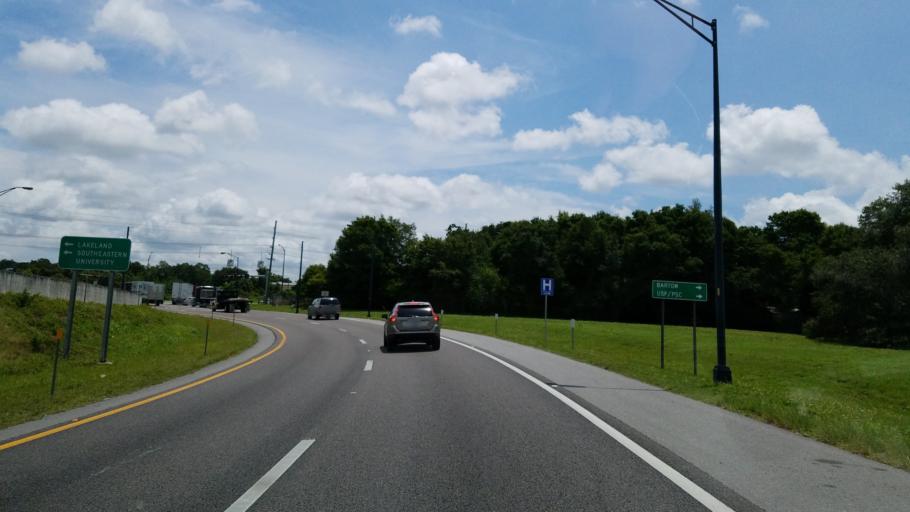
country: US
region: Florida
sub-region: Polk County
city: Crystal Lake
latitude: 27.9985
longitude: -81.9027
